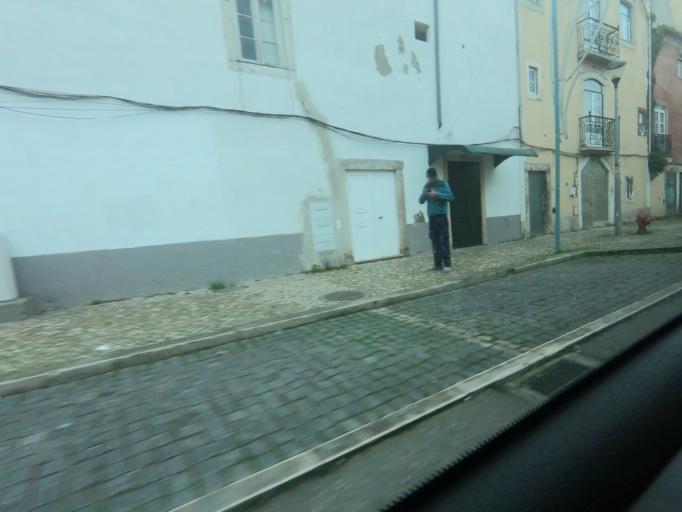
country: PT
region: Setubal
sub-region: Setubal
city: Setubal
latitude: 38.5254
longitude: -8.8932
